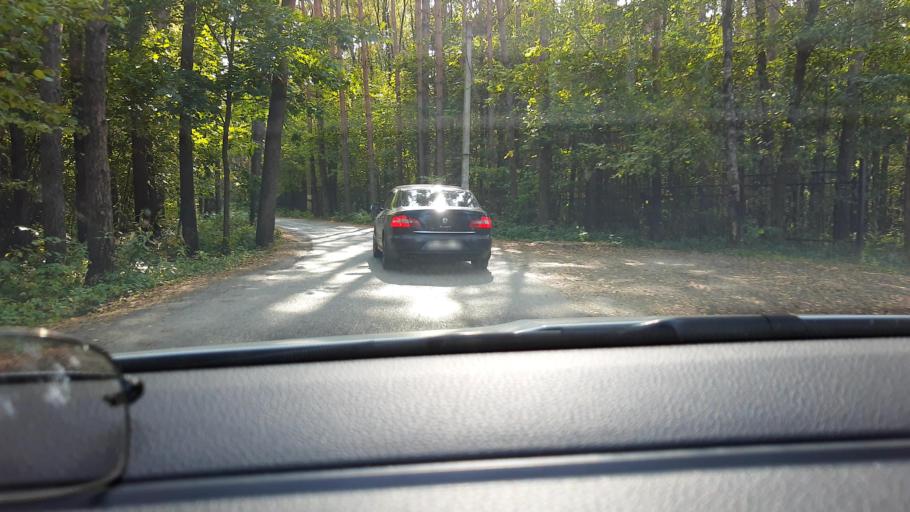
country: RU
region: Moskovskaya
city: Barvikha
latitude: 55.7209
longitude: 37.3027
